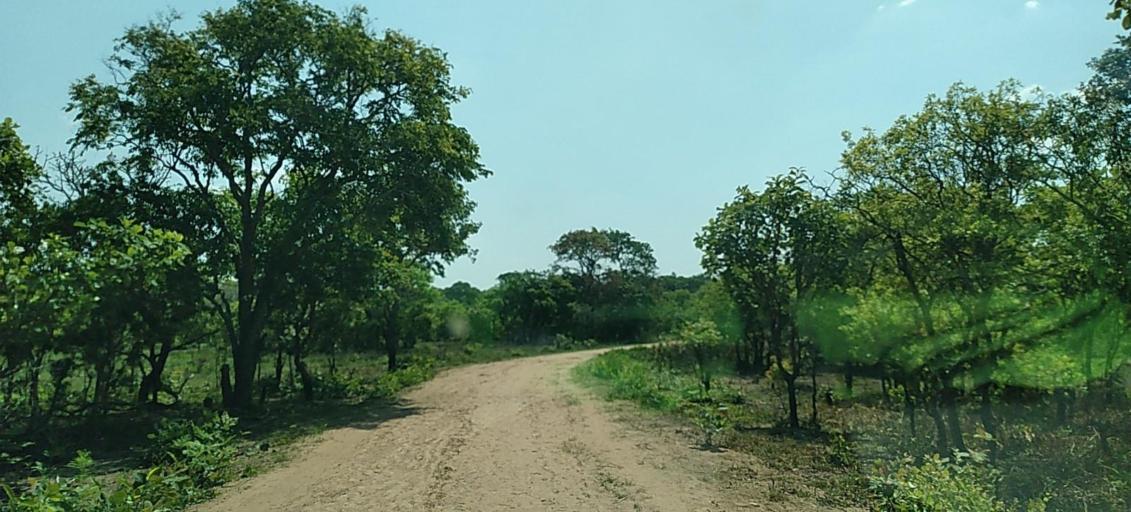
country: CD
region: Katanga
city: Kolwezi
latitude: -11.2763
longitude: 25.1123
